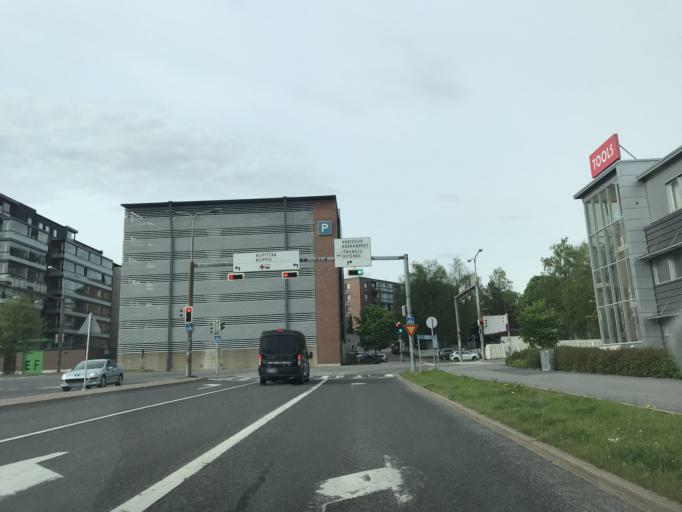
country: FI
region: Varsinais-Suomi
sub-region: Turku
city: Turku
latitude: 60.4503
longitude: 22.3012
